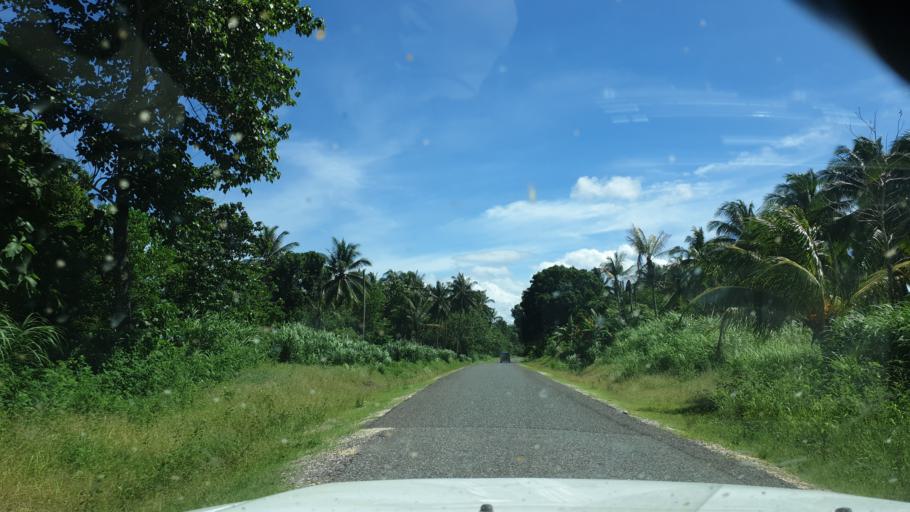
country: PG
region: Madang
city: Madang
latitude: -4.5506
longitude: 145.5033
